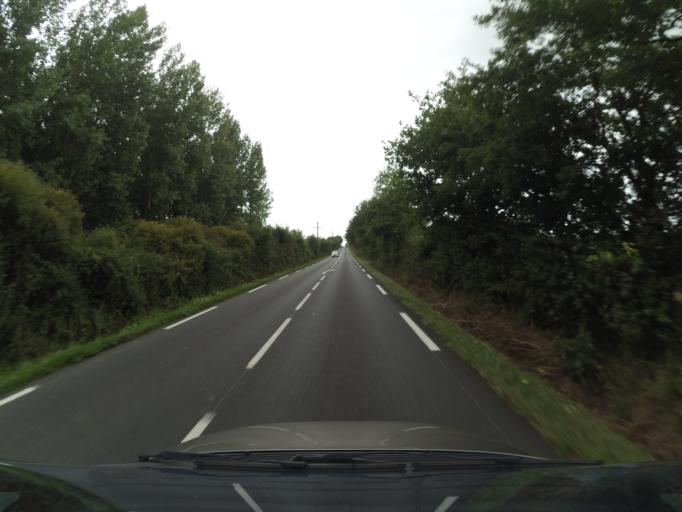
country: FR
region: Pays de la Loire
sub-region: Departement de la Vendee
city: Falleron
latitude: 46.8763
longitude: -1.7276
